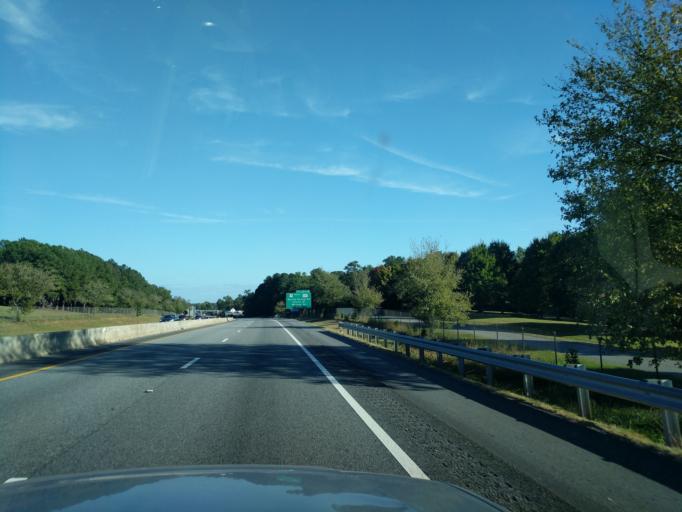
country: US
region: South Carolina
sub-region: Spartanburg County
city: Saxon
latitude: 34.9823
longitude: -81.9556
